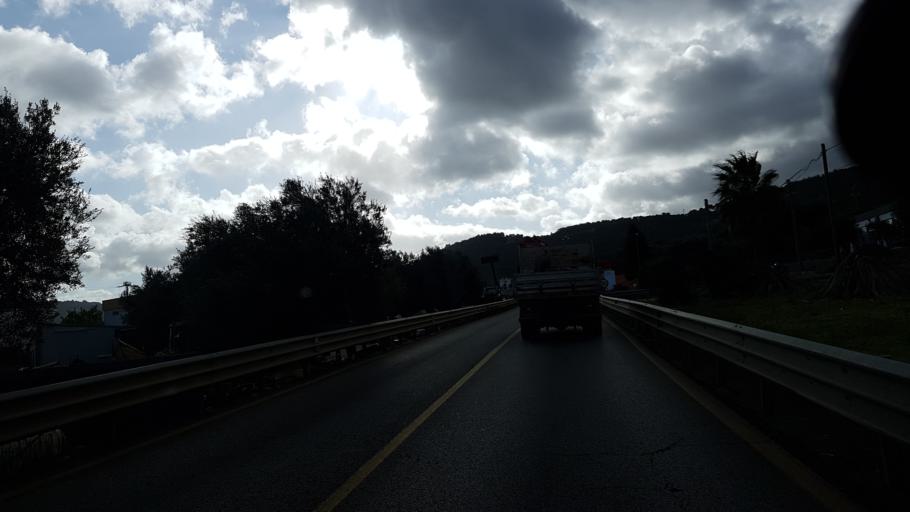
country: IT
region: Apulia
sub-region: Provincia di Brindisi
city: Lamie di Olimpie-Selva
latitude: 40.8243
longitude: 17.3487
